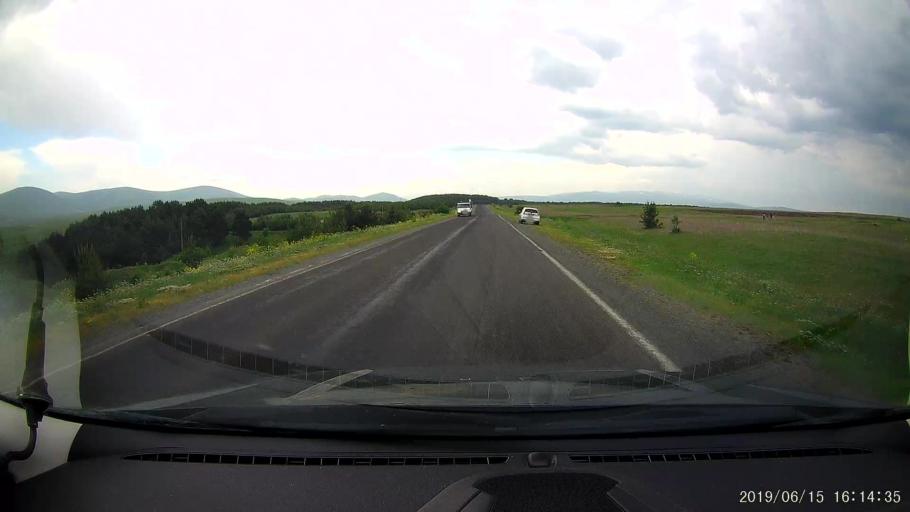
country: TR
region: Ardahan
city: Hanak
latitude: 41.2777
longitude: 42.8452
